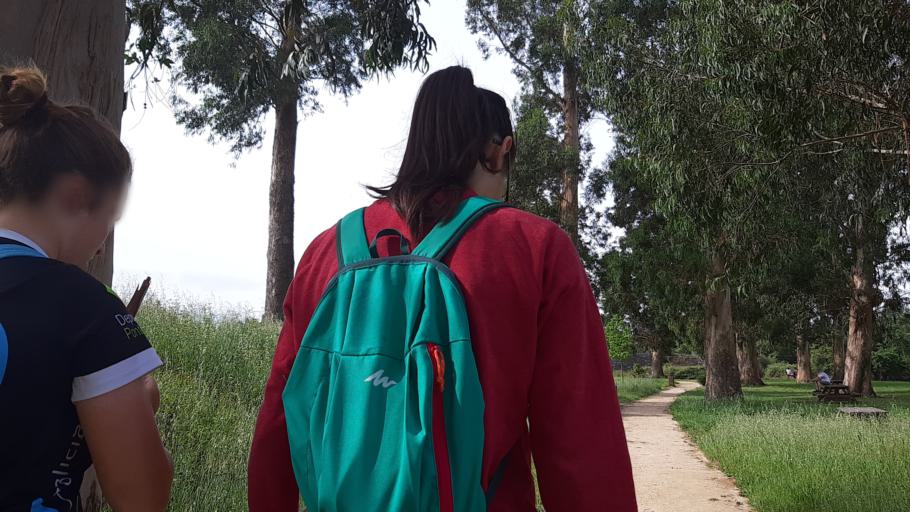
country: ES
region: Galicia
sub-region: Provincia de Pontevedra
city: O Rosal
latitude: 41.9164
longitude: -8.8274
